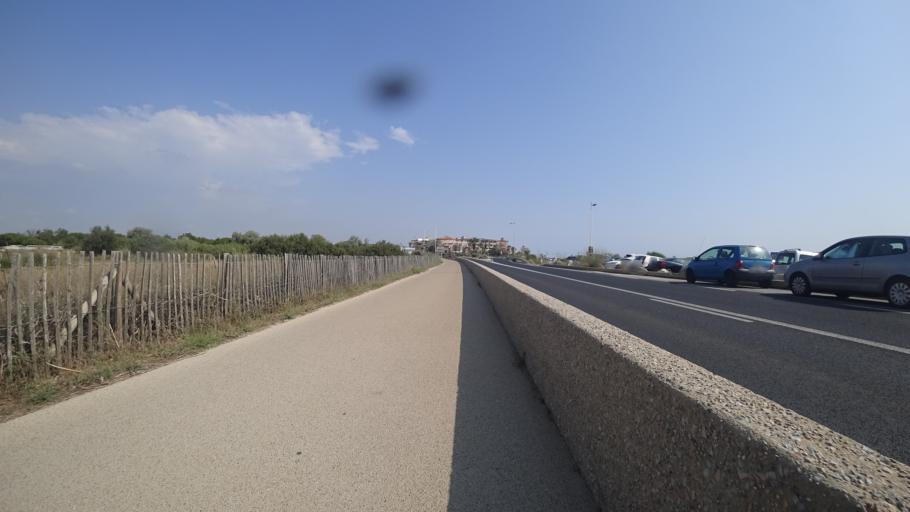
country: FR
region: Languedoc-Roussillon
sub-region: Departement des Pyrenees-Orientales
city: Canet-en-Roussillon
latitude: 42.6719
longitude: 3.0331
